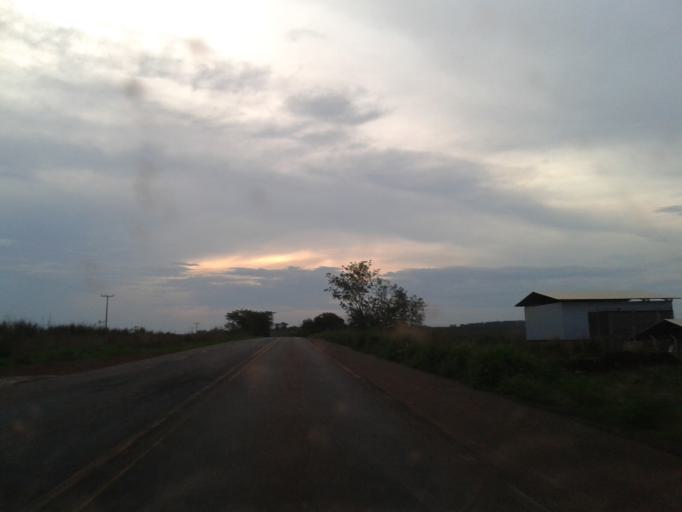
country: BR
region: Goias
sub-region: Santa Helena De Goias
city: Santa Helena de Goias
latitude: -17.8769
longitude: -50.7135
